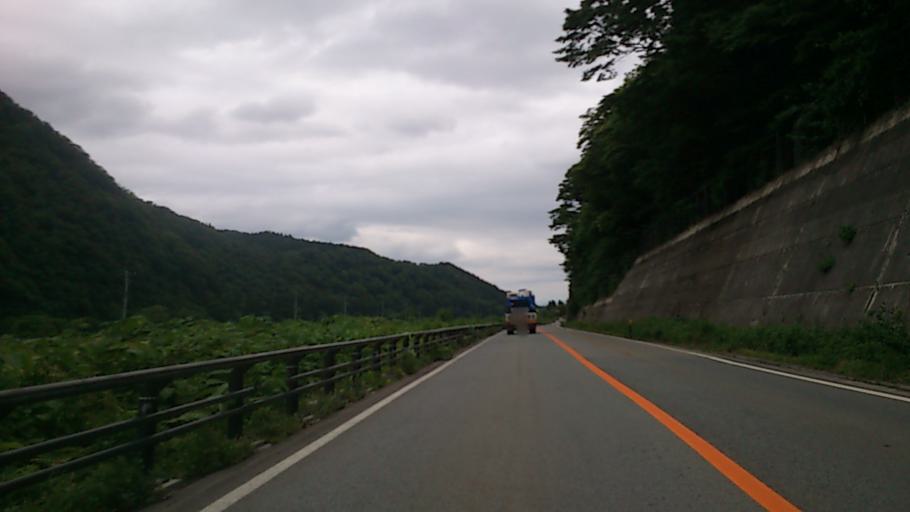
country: JP
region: Yamagata
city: Shinjo
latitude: 38.7459
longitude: 140.1169
